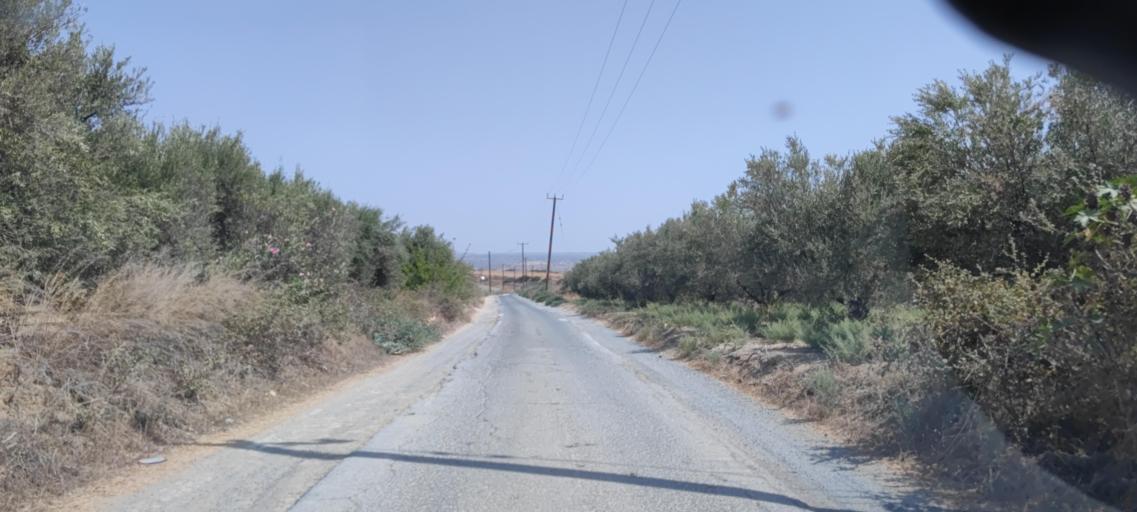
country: CY
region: Limassol
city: Pissouri
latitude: 34.6625
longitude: 32.7675
